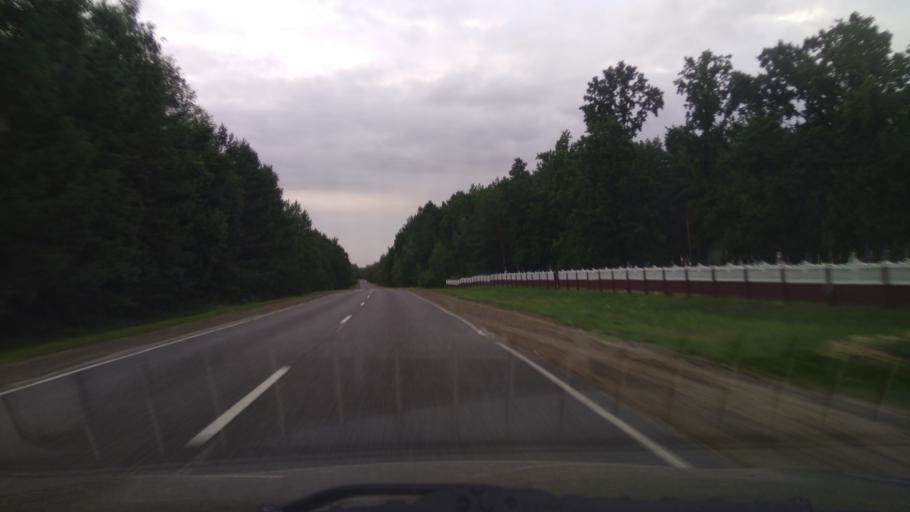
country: BY
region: Brest
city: Byaroza
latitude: 52.4053
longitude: 24.9998
